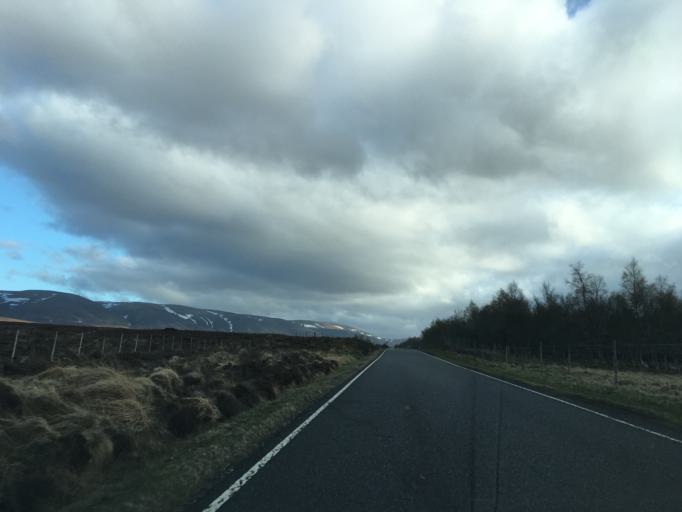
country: GB
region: Scotland
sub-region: Highland
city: Kingussie
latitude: 56.9538
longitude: -4.2443
